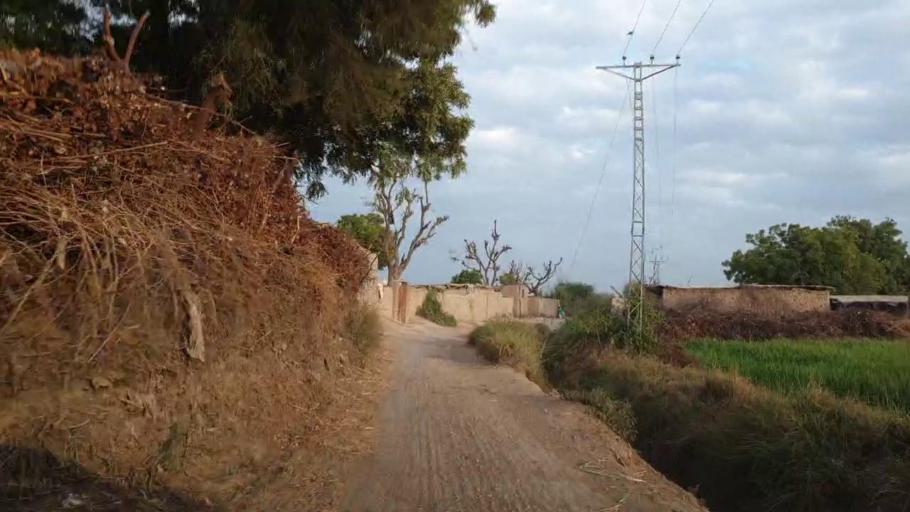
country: PK
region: Sindh
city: Matiari
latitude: 25.5704
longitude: 68.4393
